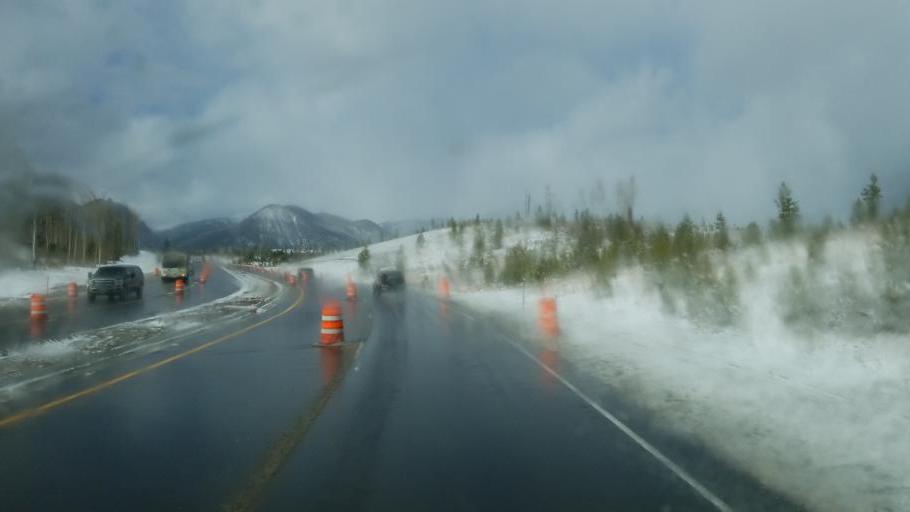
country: US
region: Colorado
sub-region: Summit County
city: Frisco
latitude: 39.5739
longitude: -106.0591
